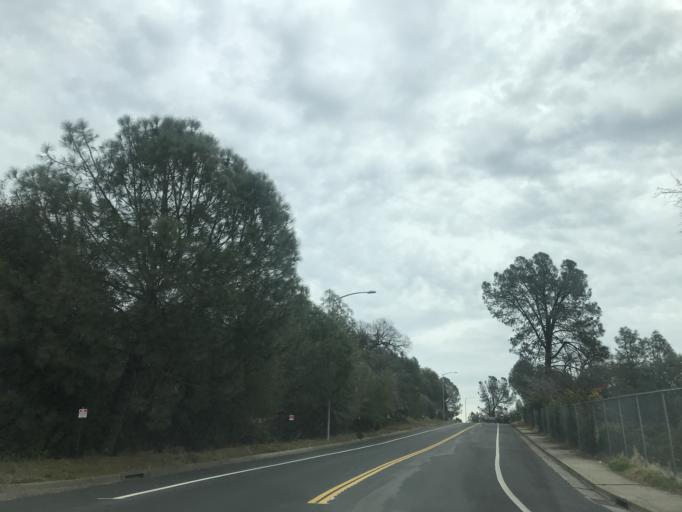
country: US
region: California
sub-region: El Dorado County
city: Placerville
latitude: 38.7297
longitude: -120.8317
